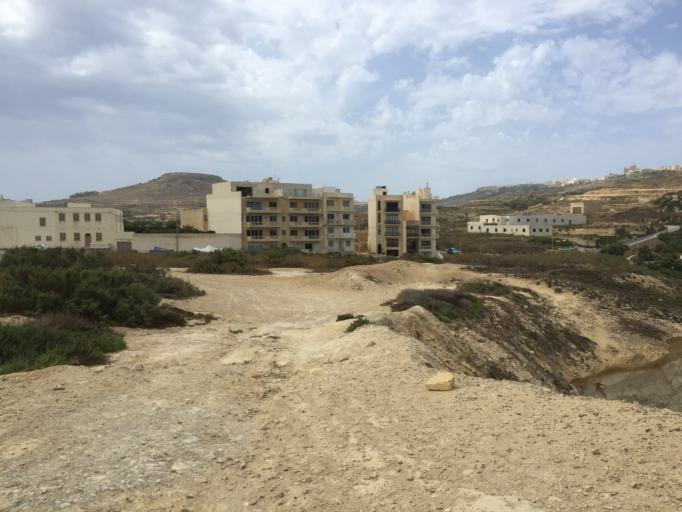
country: MT
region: Iz-Zebbug
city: Zebbug
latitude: 36.0792
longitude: 14.2498
